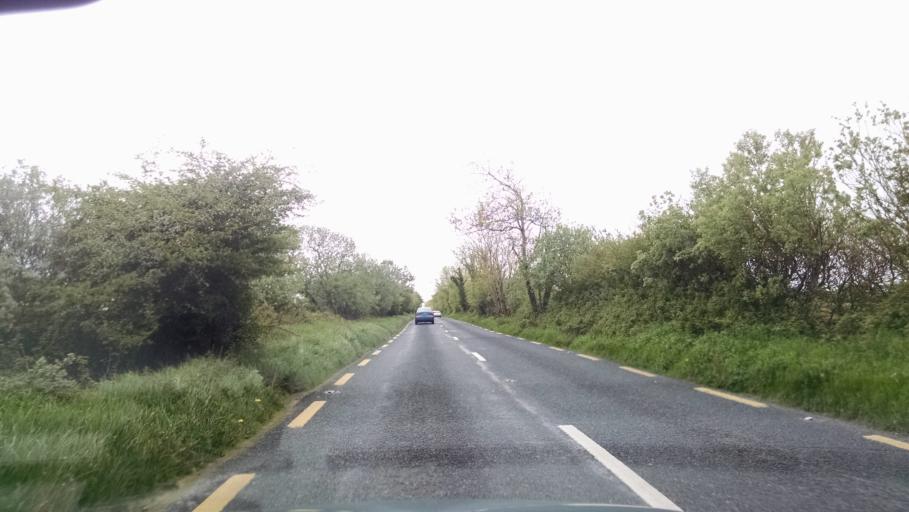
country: IE
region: Connaught
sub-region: County Galway
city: Claregalway
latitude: 53.3941
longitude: -9.0172
